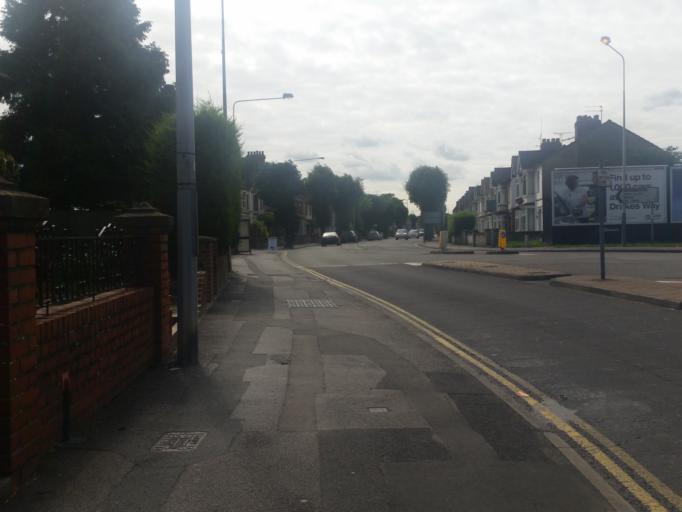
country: GB
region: England
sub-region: Borough of Swindon
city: Swindon
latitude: 51.5665
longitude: -1.7751
